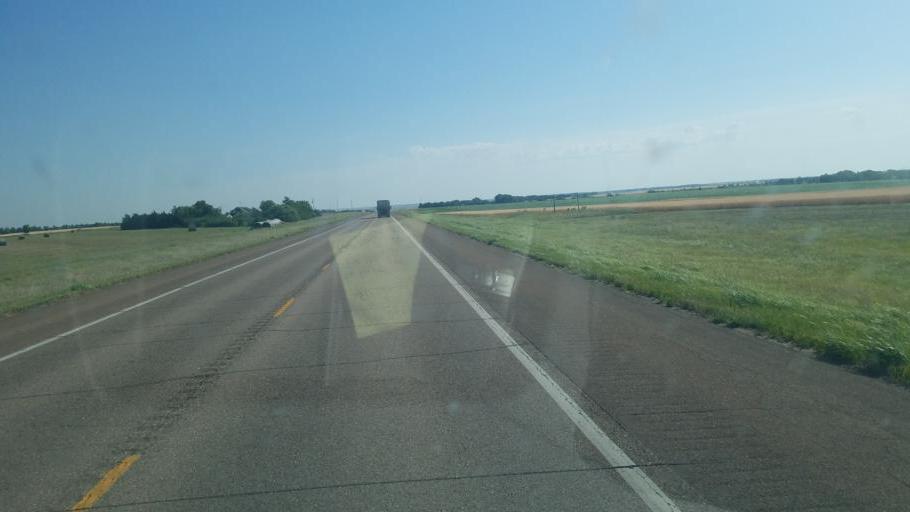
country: US
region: Kansas
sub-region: Barton County
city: Great Bend
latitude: 38.3942
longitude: -98.6742
